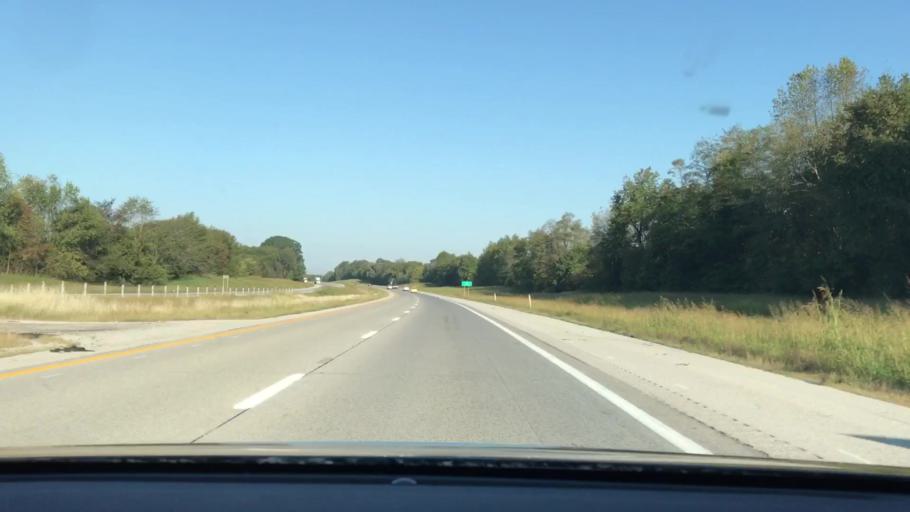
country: US
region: Kentucky
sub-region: Trigg County
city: Cadiz
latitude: 36.8415
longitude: -87.6727
